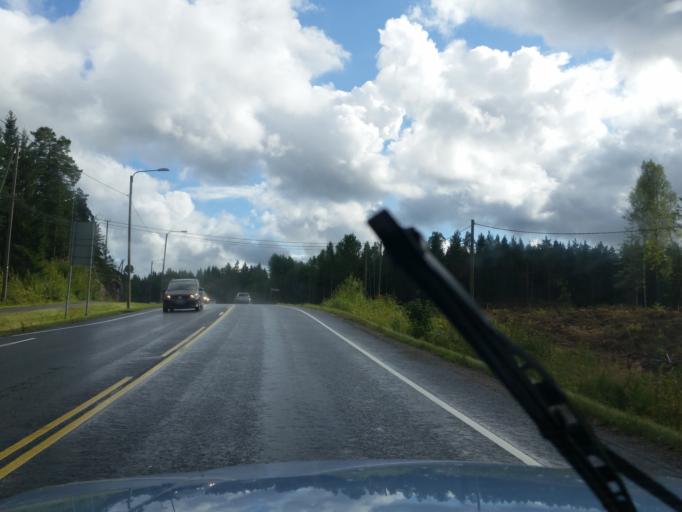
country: FI
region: Varsinais-Suomi
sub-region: Turku
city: Kaarina
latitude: 60.3468
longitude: 22.3605
